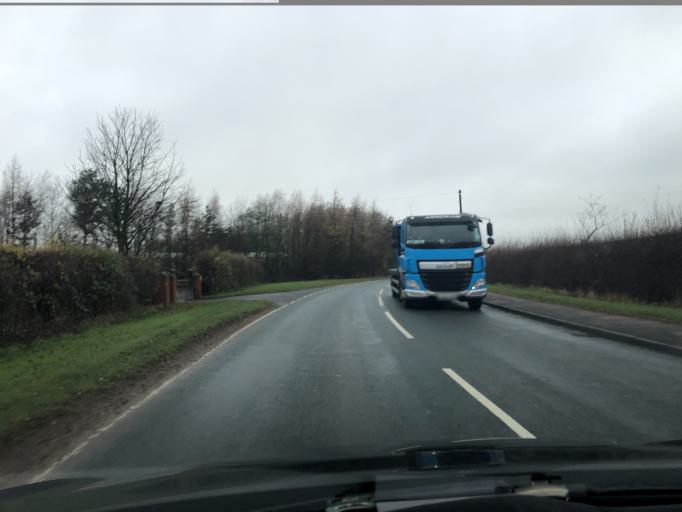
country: GB
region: England
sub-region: North Yorkshire
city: Stokesley
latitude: 54.4659
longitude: -1.1739
